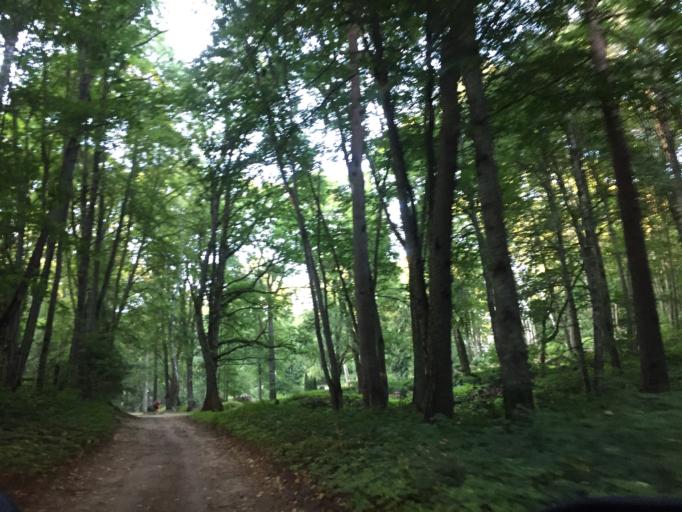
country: LV
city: Tervete
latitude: 56.4778
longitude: 23.3767
